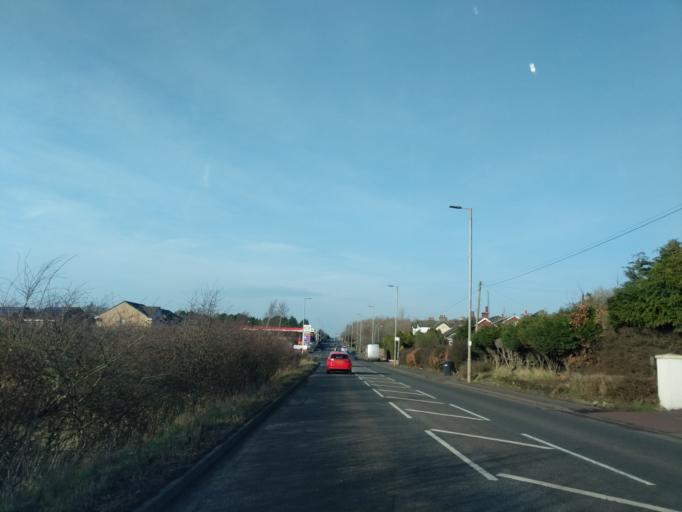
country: GB
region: Scotland
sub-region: South Lanarkshire
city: Carluke
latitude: 55.7102
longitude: -3.8310
